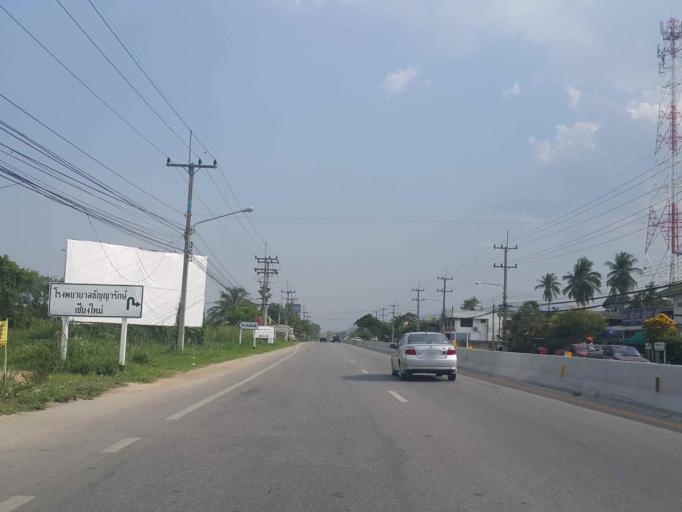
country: TH
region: Chiang Mai
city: Mae Taeng
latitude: 19.0152
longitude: 98.9445
